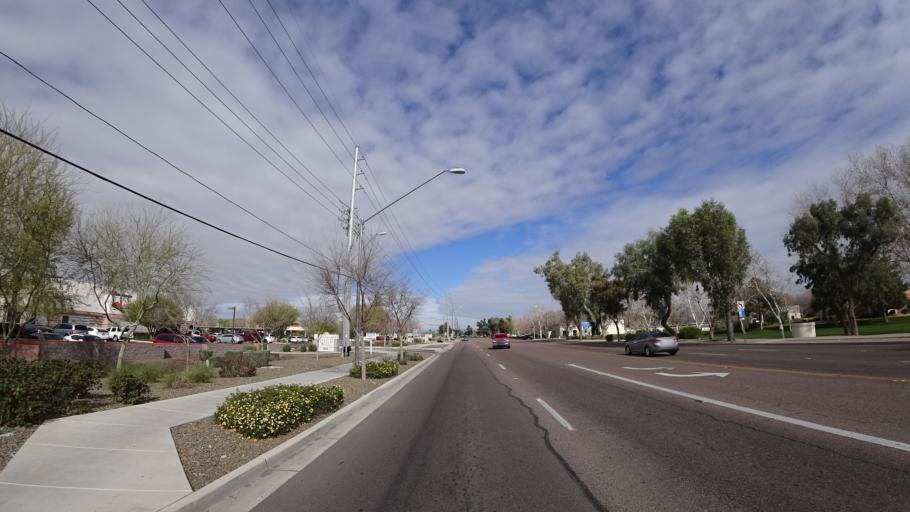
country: US
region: Arizona
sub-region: Maricopa County
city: Peoria
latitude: 33.6326
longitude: -112.1858
